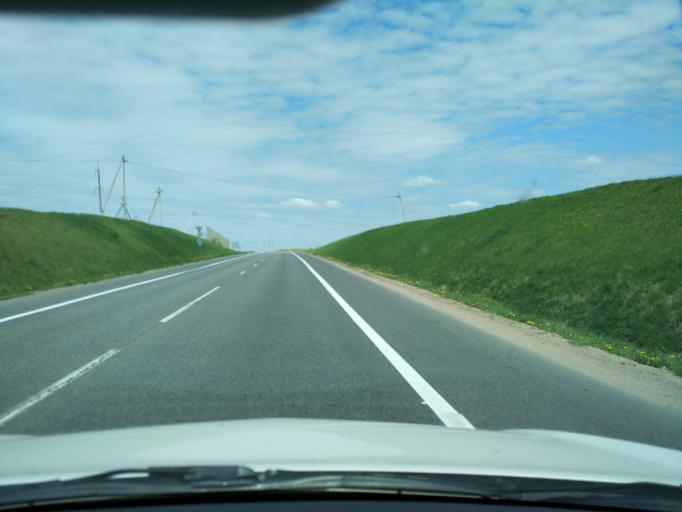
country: BY
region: Grodnenskaya
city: Ashmyany
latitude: 54.4416
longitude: 25.9680
